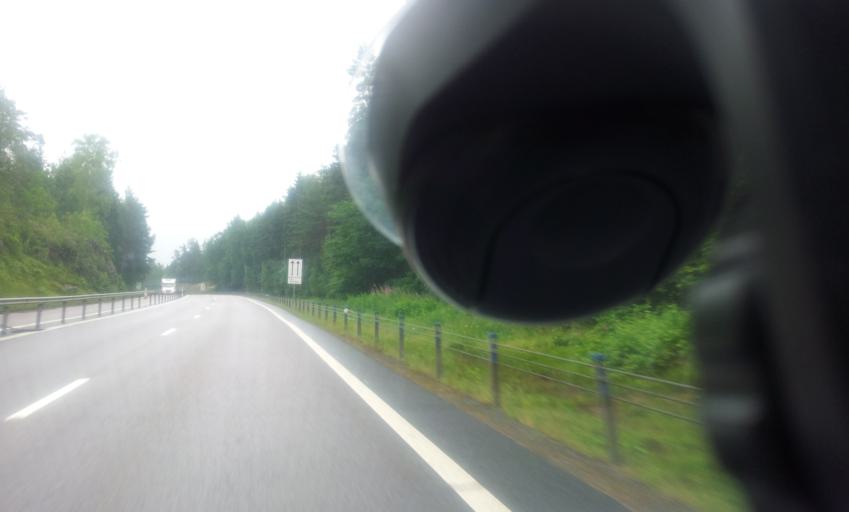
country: SE
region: Kalmar
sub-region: Vasterviks Kommun
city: Forserum
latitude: 58.0313
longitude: 16.5150
